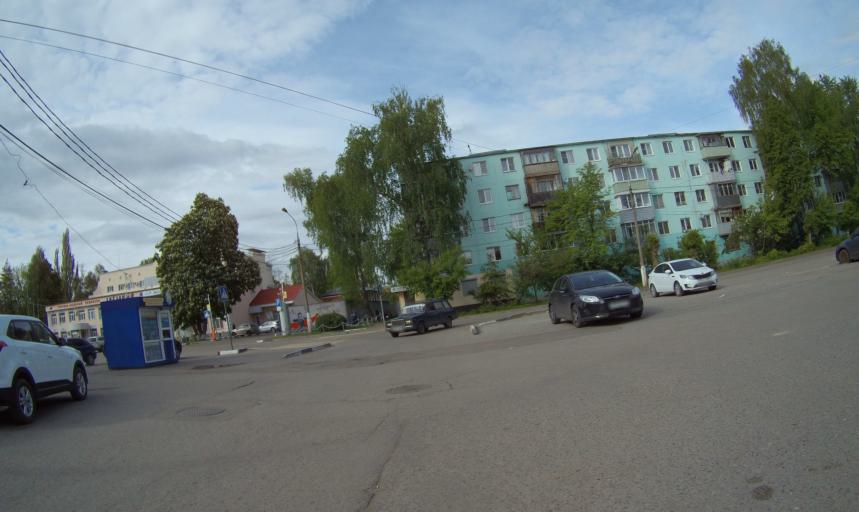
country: RU
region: Moskovskaya
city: Kolomna
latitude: 55.0903
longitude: 38.7711
